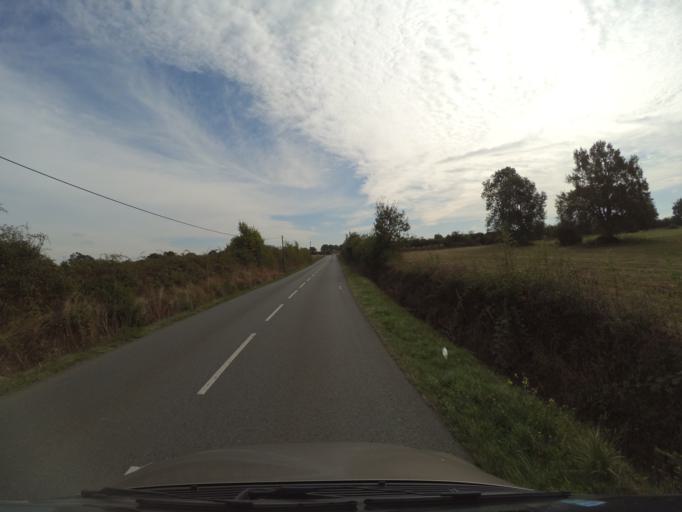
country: FR
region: Pays de la Loire
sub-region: Departement de Maine-et-Loire
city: Melay
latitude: 47.2095
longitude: -0.6755
